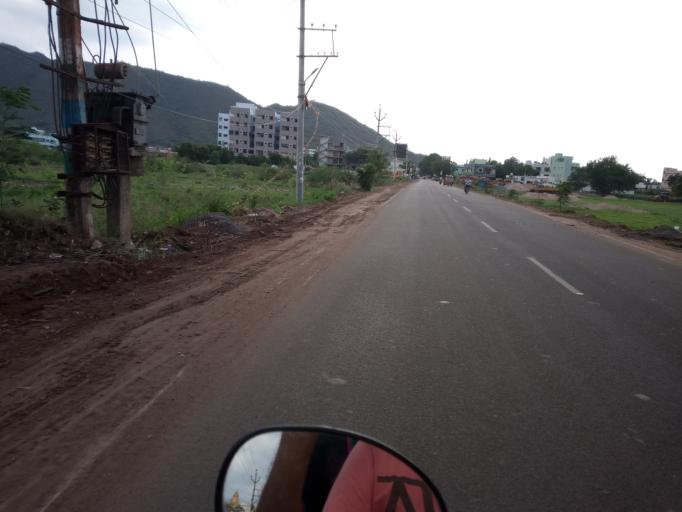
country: IN
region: Andhra Pradesh
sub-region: Guntur
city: Tadepalle
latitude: 16.4941
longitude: 80.5927
